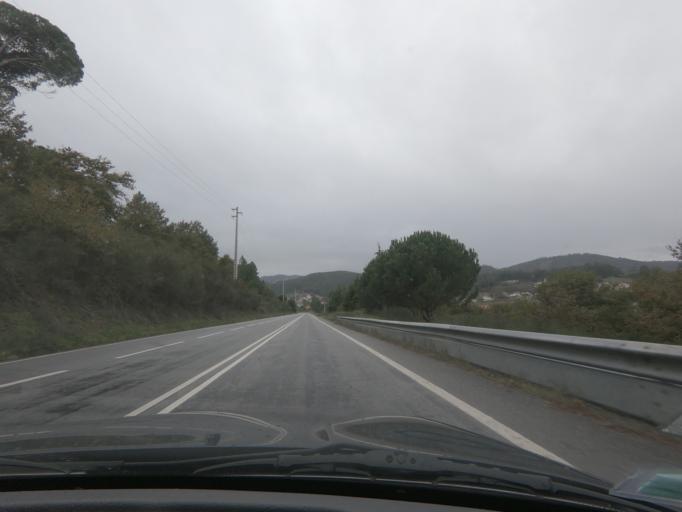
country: PT
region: Porto
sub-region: Amarante
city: Teloes
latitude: 41.2972
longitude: -8.0918
